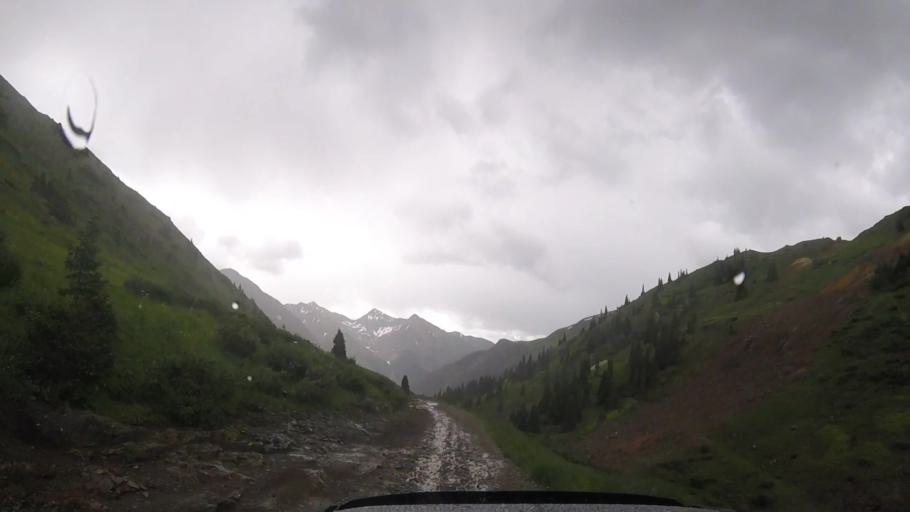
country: US
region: Colorado
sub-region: Ouray County
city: Ouray
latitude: 37.9391
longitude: -107.5734
